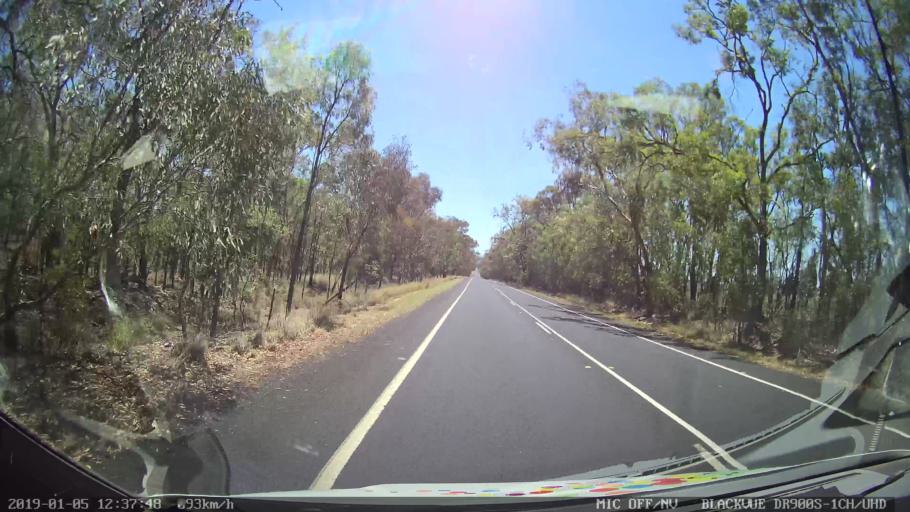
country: AU
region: New South Wales
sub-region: Warrumbungle Shire
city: Coonabarabran
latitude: -31.2010
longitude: 149.4599
